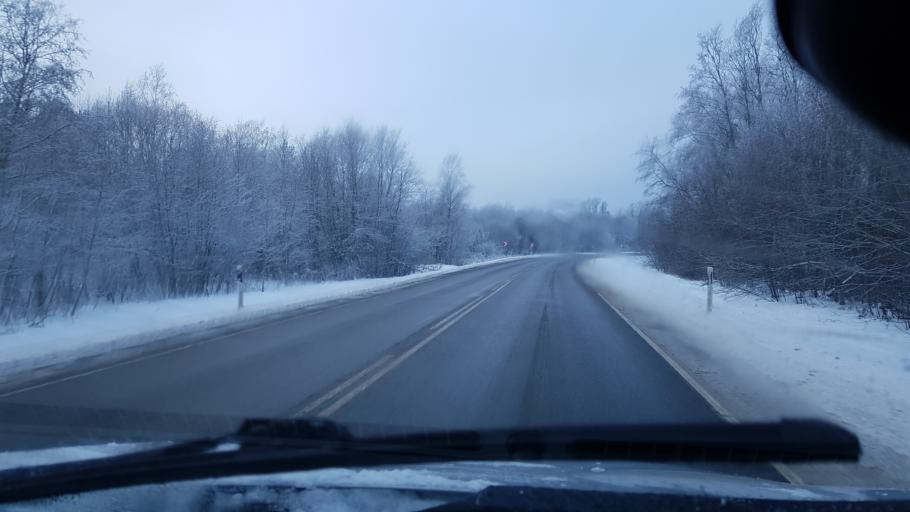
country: EE
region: Harju
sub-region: Paldiski linn
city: Paldiski
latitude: 59.3396
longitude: 24.2063
